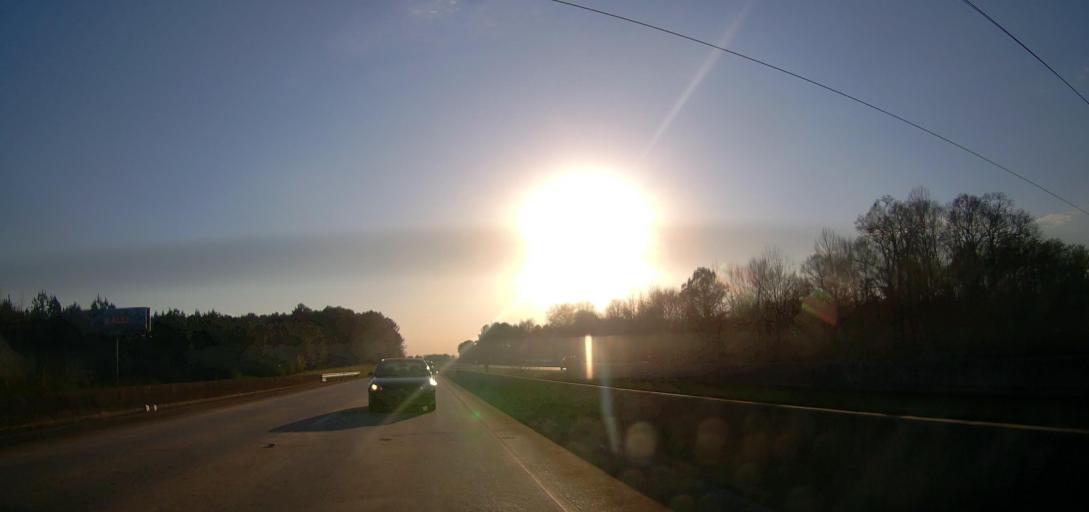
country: US
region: Alabama
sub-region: Shelby County
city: Westover
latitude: 33.3531
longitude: -86.5258
